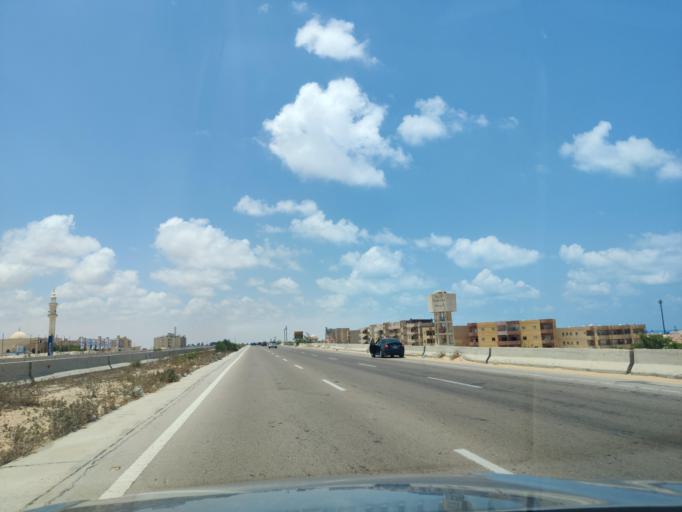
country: EG
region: Muhafazat Matruh
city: Al `Alamayn
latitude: 30.8355
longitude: 29.2375
